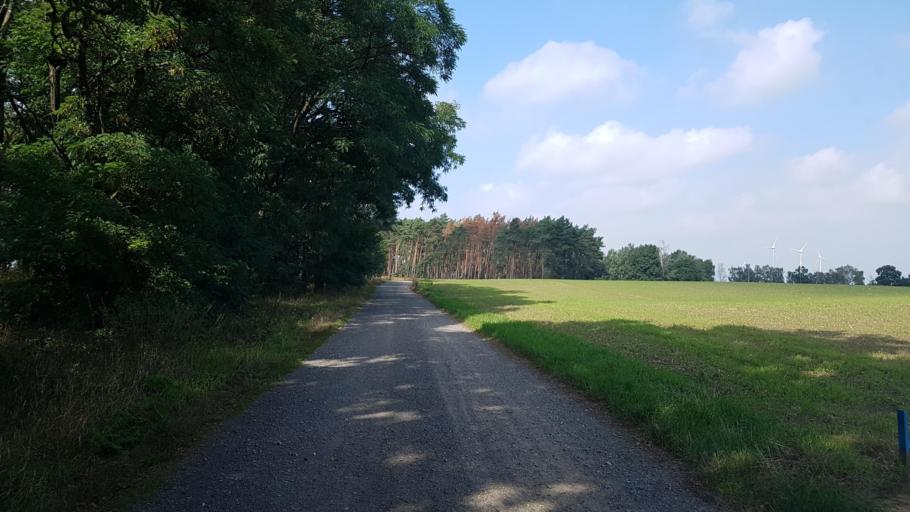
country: DE
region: Brandenburg
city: Luckau
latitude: 51.8252
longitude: 13.6814
